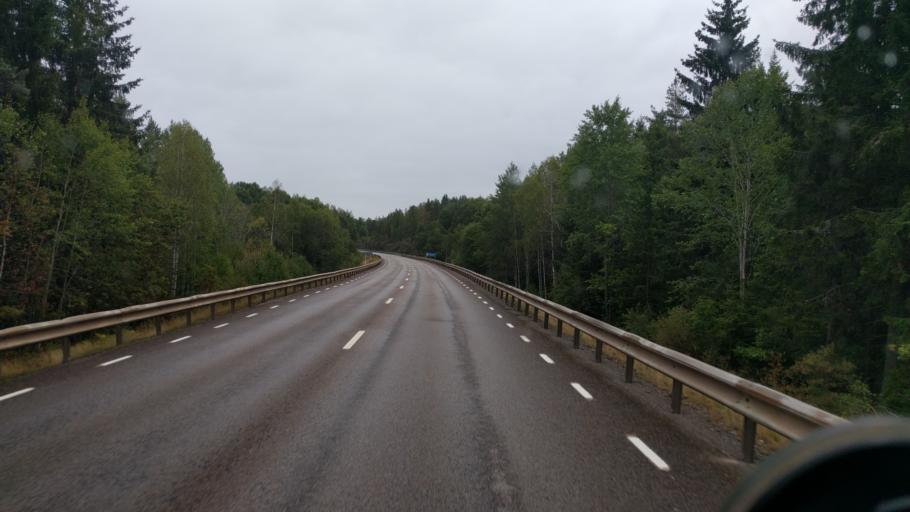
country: SE
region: Kalmar
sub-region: Vasterviks Kommun
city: Ankarsrum
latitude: 57.7008
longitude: 16.1776
